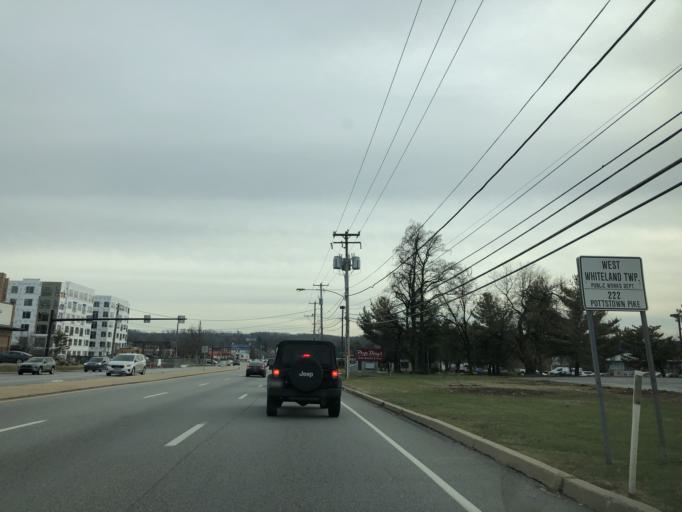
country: US
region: Pennsylvania
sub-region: Chester County
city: Exton
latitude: 40.0326
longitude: -75.6315
